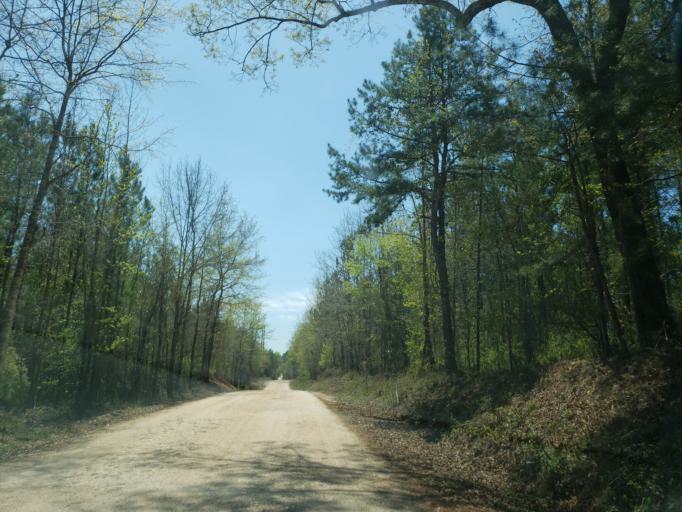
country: US
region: Alabama
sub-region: Tallapoosa County
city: Camp Hill
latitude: 32.6731
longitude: -85.6624
